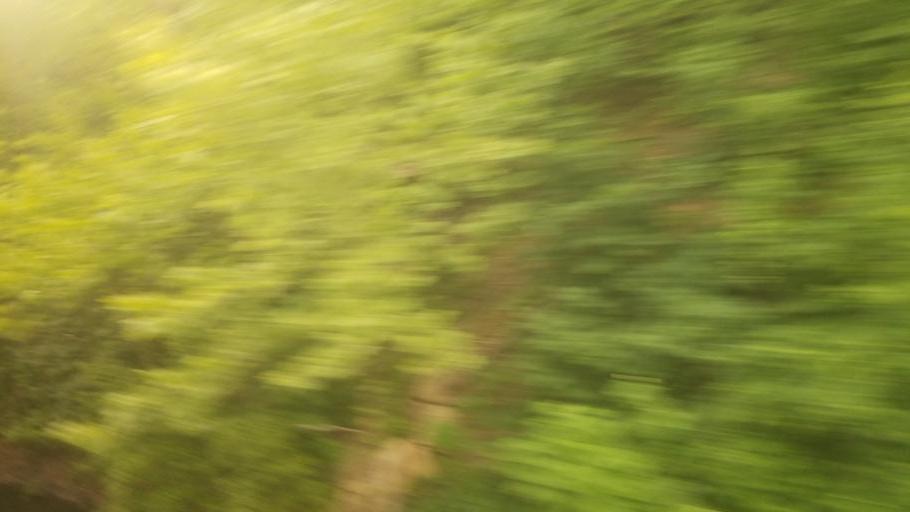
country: US
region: Kansas
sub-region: Shawnee County
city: Topeka
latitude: 39.0541
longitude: -95.4875
